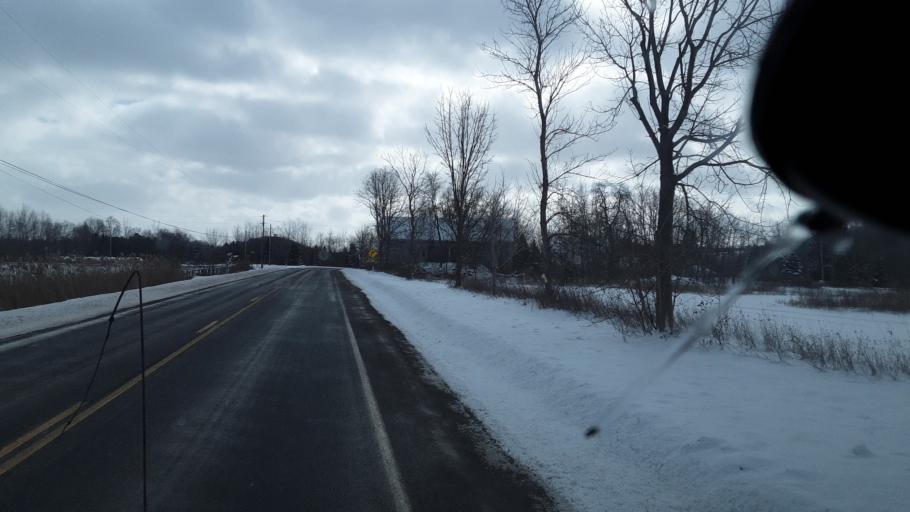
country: US
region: New York
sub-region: Wayne County
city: Newark
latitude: 43.0928
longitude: -77.0537
